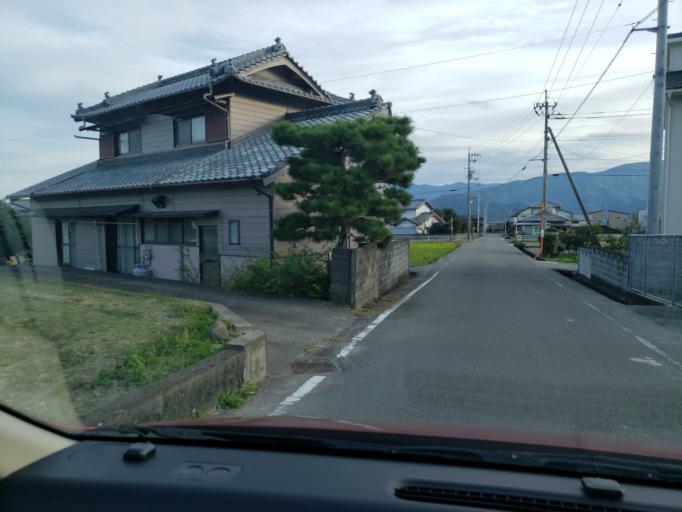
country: JP
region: Tokushima
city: Wakimachi
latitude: 34.0904
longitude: 134.2261
